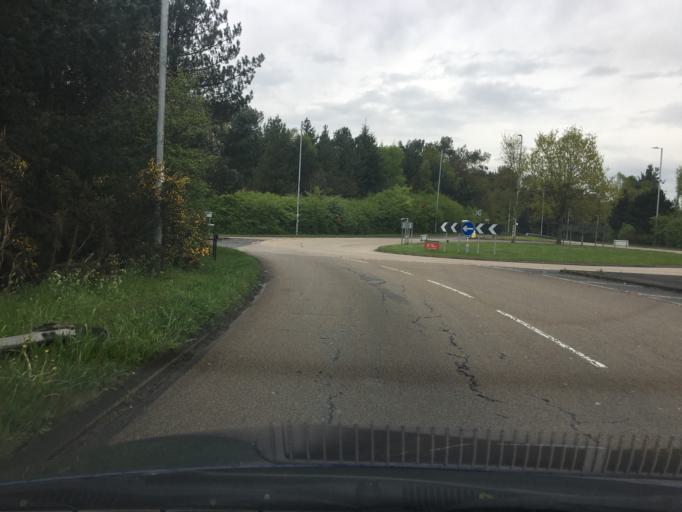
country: GB
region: England
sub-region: Bracknell Forest
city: Crowthorne
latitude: 51.3821
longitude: -0.7738
